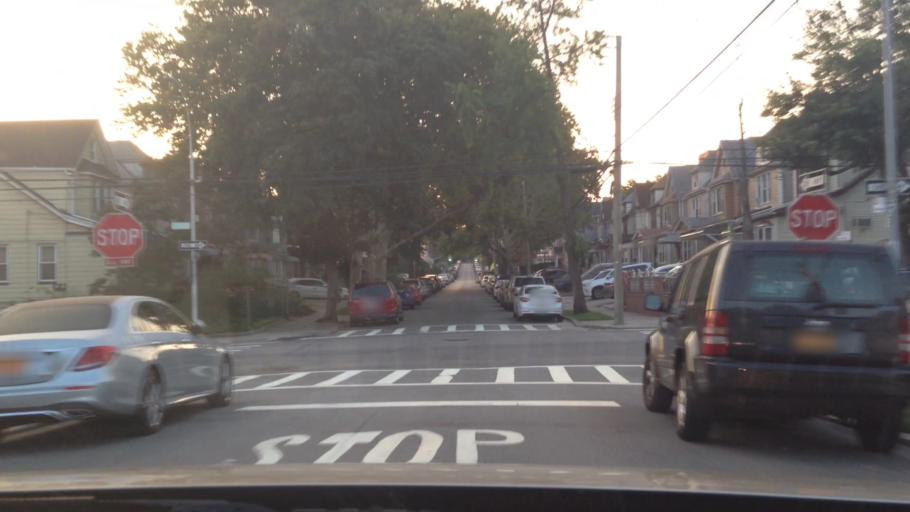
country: US
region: New York
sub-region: Queens County
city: Borough of Queens
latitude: 40.7296
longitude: -73.8658
